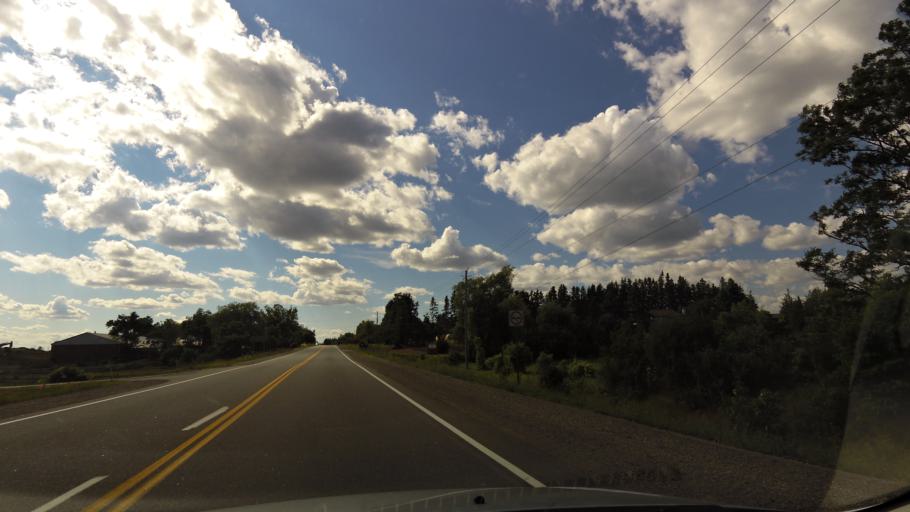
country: CA
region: Ontario
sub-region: Wellington County
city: Guelph
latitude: 43.4276
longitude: -80.0841
